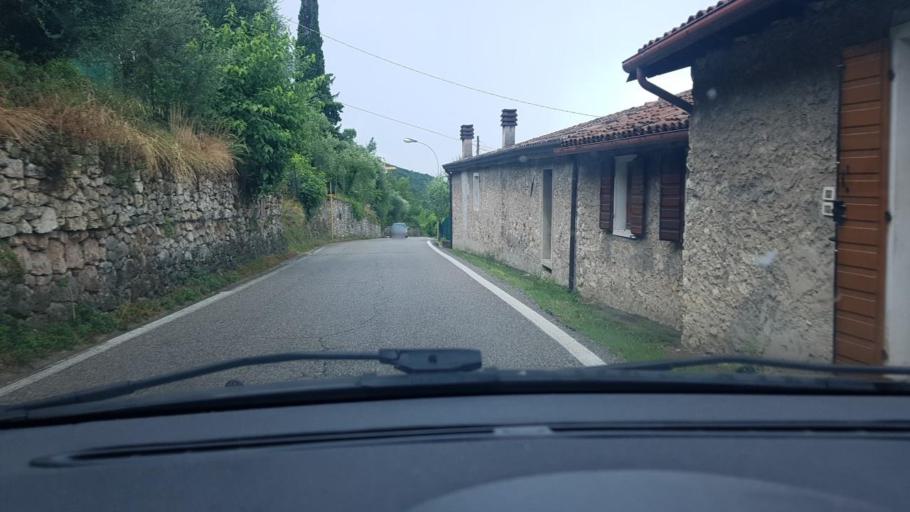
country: IT
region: Veneto
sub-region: Provincia di Verona
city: Torri del Benaco
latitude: 45.6038
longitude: 10.6923
